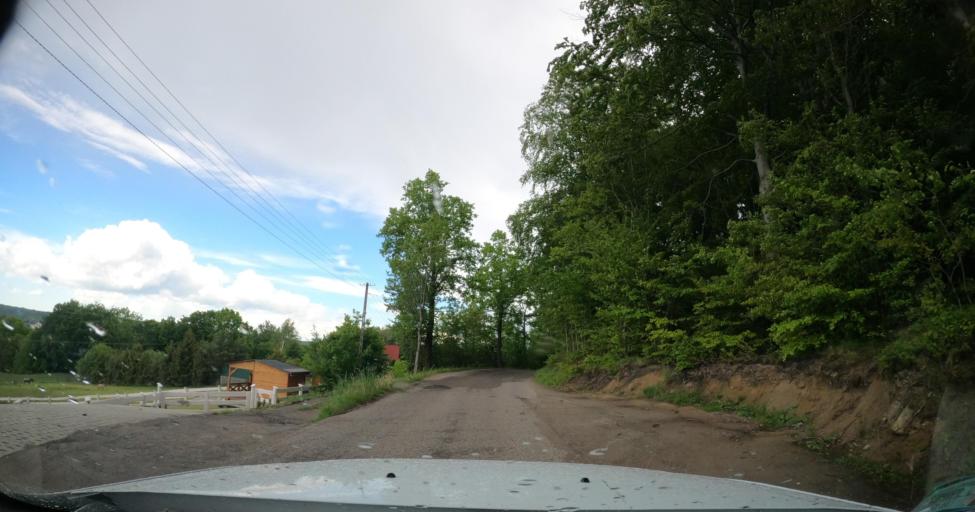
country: PL
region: Pomeranian Voivodeship
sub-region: Powiat kartuski
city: Garcz
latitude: 54.3438
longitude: 18.1461
